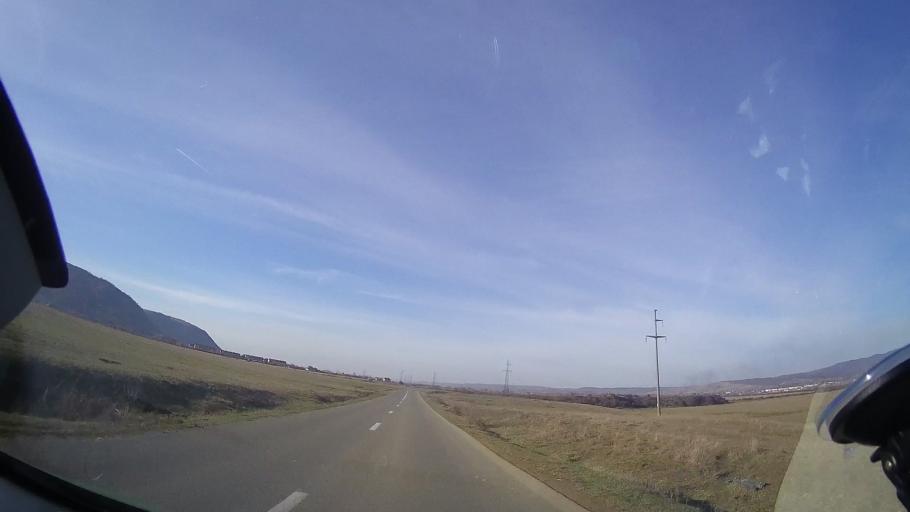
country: RO
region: Bihor
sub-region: Comuna Astileu
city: Astileu
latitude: 47.0226
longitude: 22.4141
